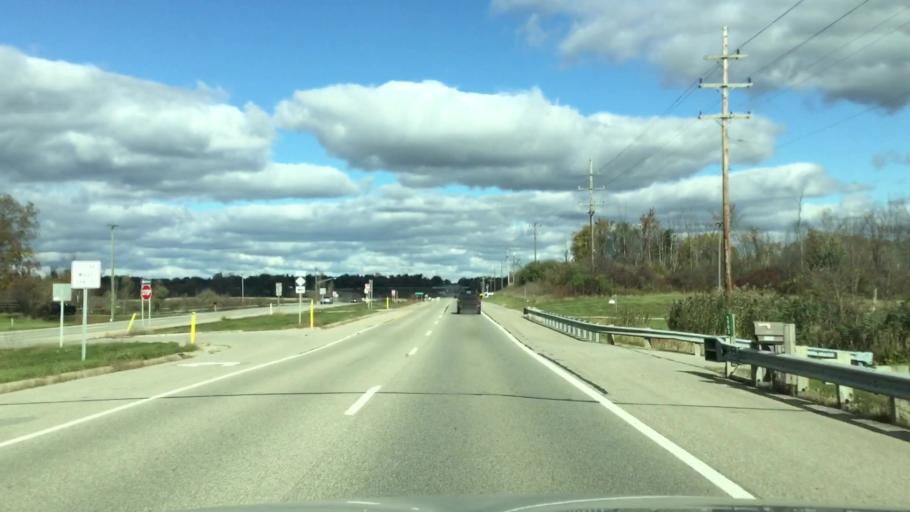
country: US
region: Michigan
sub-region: Lapeer County
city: Lapeer
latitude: 43.0111
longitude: -83.3217
